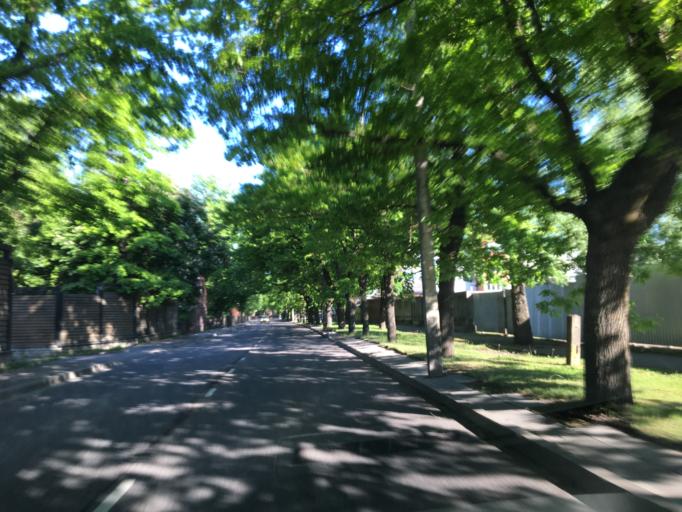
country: EE
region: Tartu
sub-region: Tartu linn
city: Tartu
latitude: 58.3947
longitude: 26.7155
